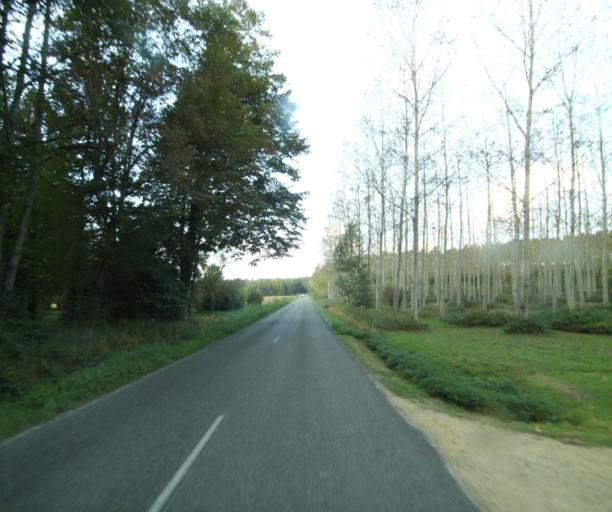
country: FR
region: Midi-Pyrenees
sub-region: Departement du Gers
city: Cazaubon
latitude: 43.9256
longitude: -0.0758
